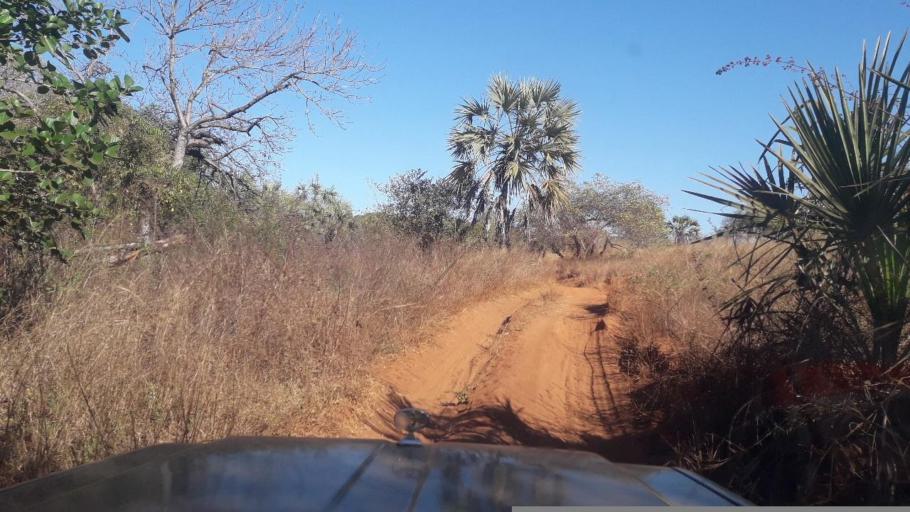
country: MG
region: Boeny
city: Sitampiky
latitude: -16.4039
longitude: 45.5981
